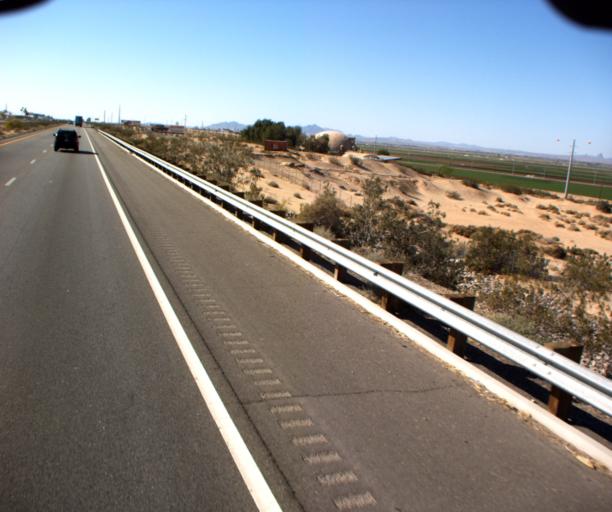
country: US
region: Arizona
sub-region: Yuma County
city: Yuma
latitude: 32.6782
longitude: -114.5461
